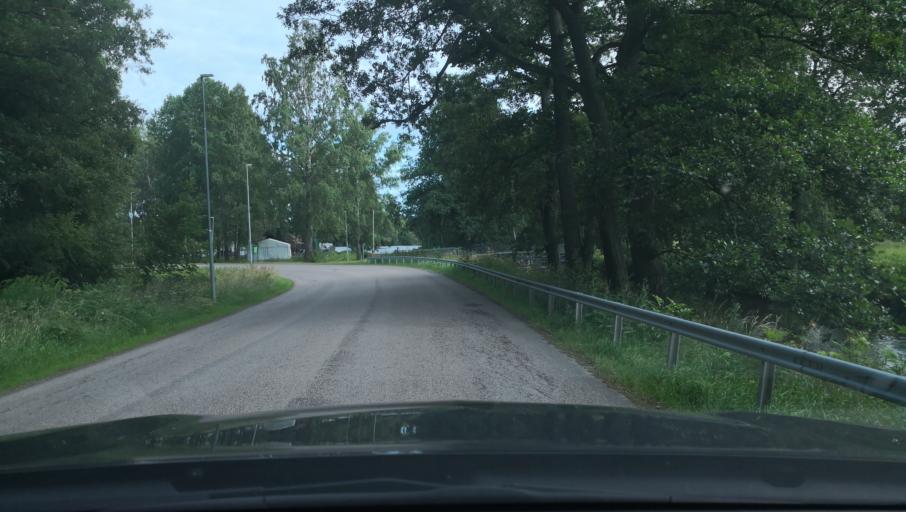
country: SE
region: Vaestmanland
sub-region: Hallstahammars Kommun
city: Hallstahammar
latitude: 59.6175
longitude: 16.2077
